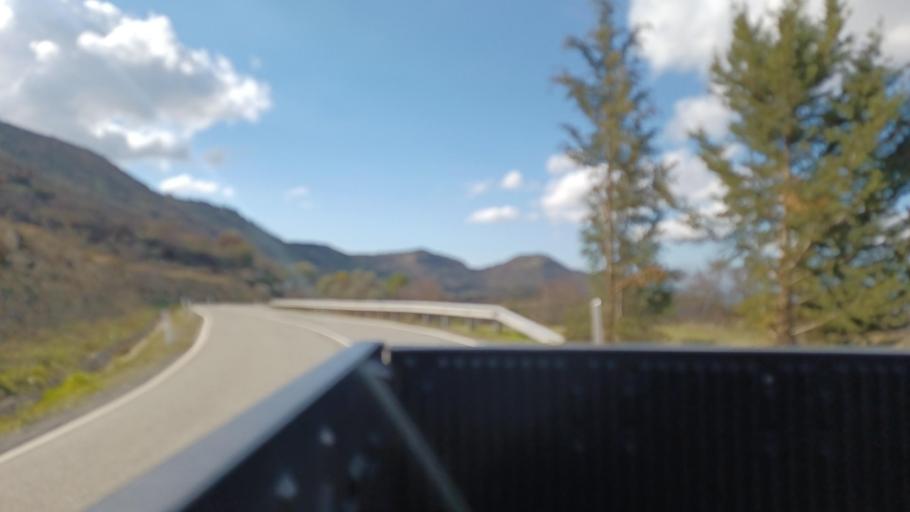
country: CY
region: Limassol
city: Pachna
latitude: 34.7782
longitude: 32.7271
